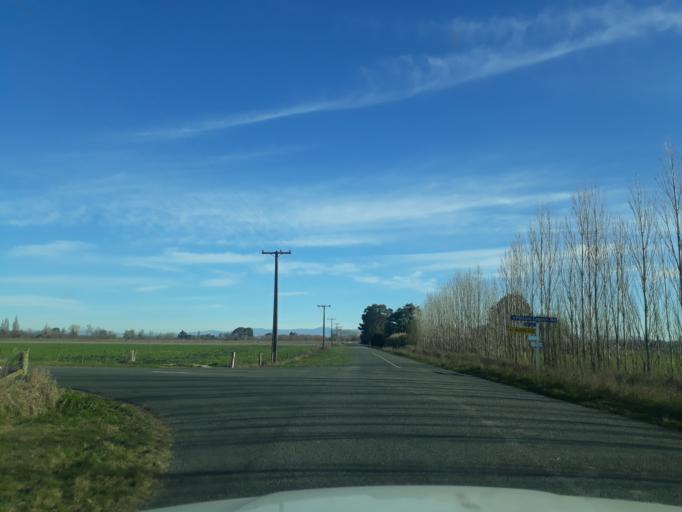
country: NZ
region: Canterbury
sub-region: Timaru District
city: Timaru
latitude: -44.2653
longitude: 171.3351
